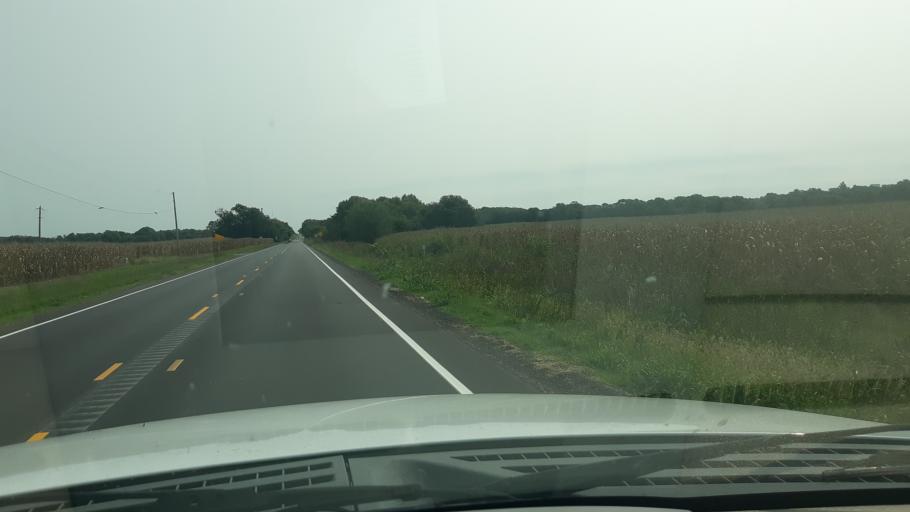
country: US
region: Indiana
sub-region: Gibson County
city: Princeton
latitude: 38.3557
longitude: -87.6334
